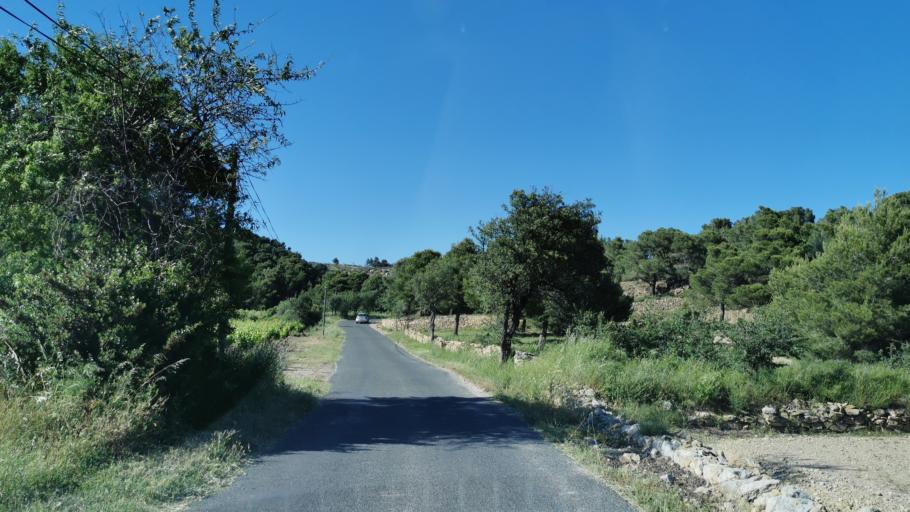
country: FR
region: Languedoc-Roussillon
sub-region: Departement de l'Aude
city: Gruissan
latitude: 43.1256
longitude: 3.0953
